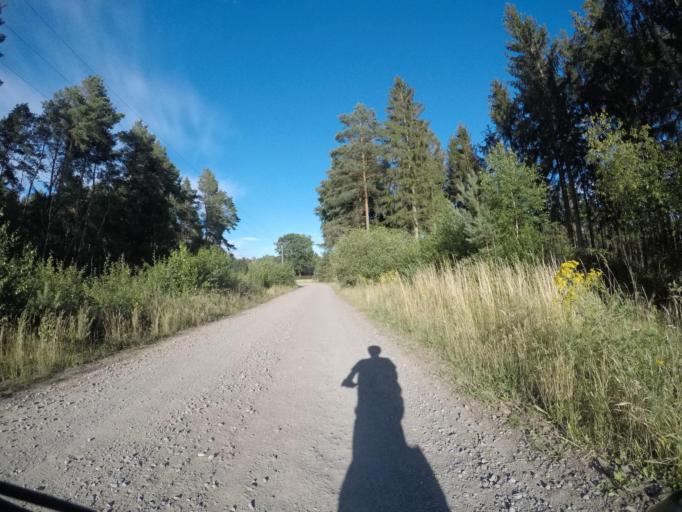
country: DE
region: Mecklenburg-Vorpommern
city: Lubtheen
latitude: 53.2370
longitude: 11.0320
